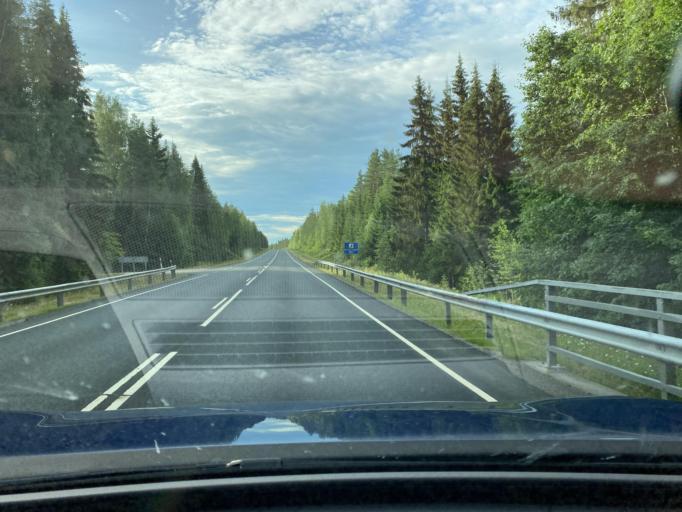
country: FI
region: Central Ostrobothnia
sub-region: Kaustinen
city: Veteli
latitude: 63.4164
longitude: 23.9448
